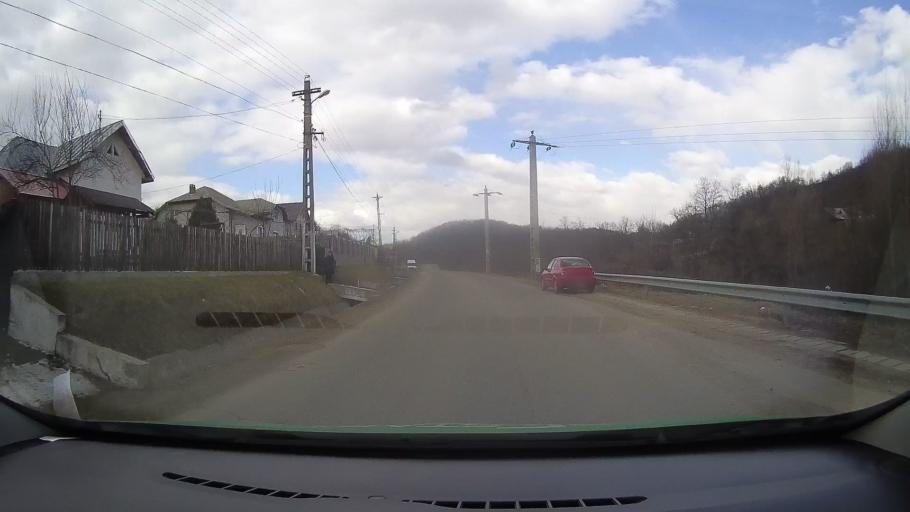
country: RO
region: Dambovita
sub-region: Comuna Valea Lunga
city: Valea Lunga-Cricov
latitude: 45.0652
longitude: 25.5559
